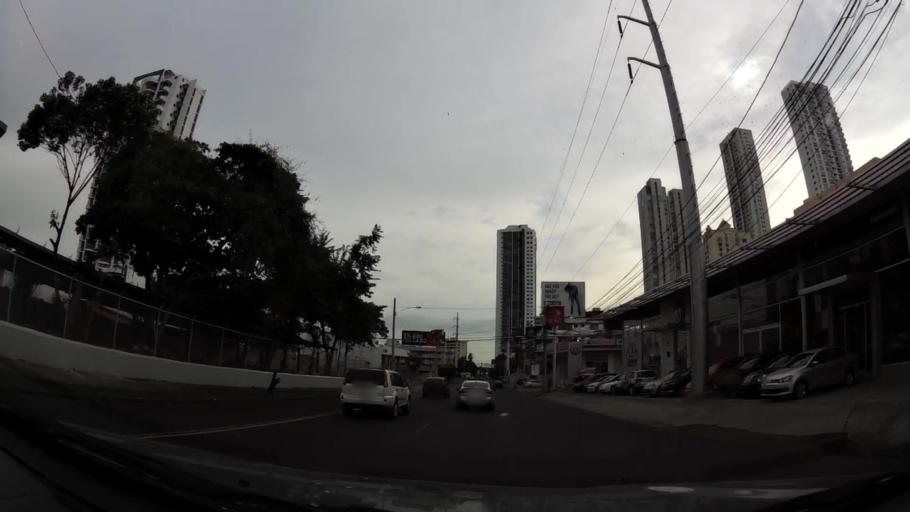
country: PA
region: Panama
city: Panama
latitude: 8.9937
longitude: -79.5005
